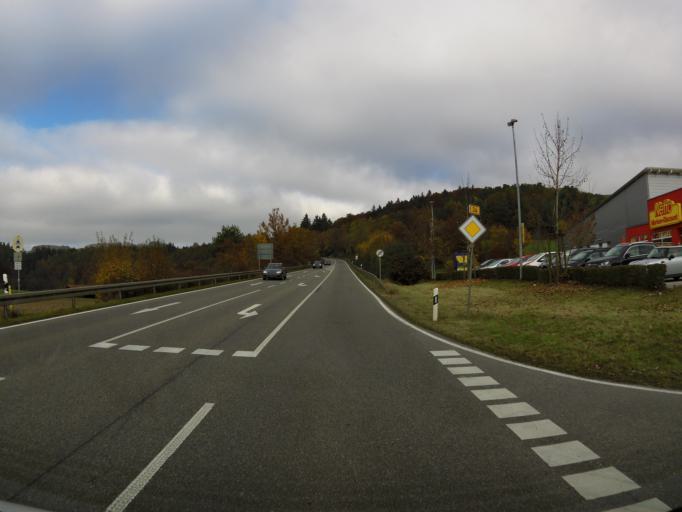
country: DE
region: Baden-Wuerttemberg
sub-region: Freiburg Region
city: Radolfzell am Bodensee
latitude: 47.7720
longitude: 8.9827
